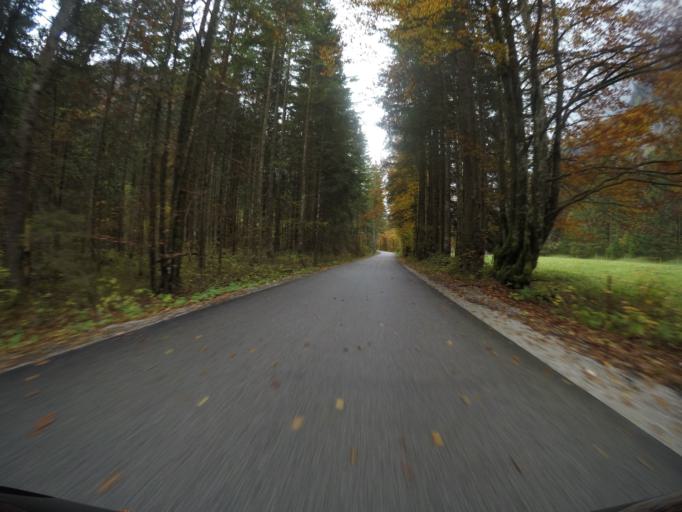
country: SI
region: Jesenice
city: Hrusica
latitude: 46.4130
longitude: 13.9938
